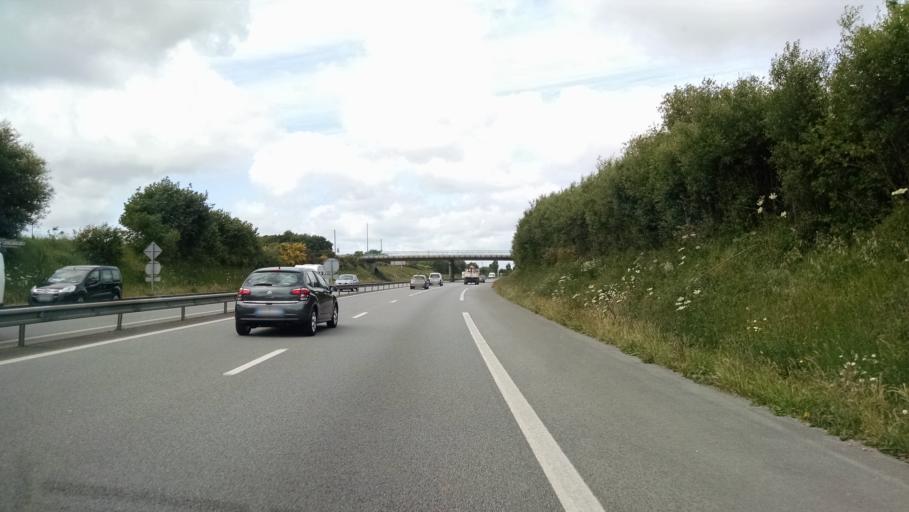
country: FR
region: Brittany
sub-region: Departement du Morbihan
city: Auray
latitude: 47.6590
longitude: -3.0037
